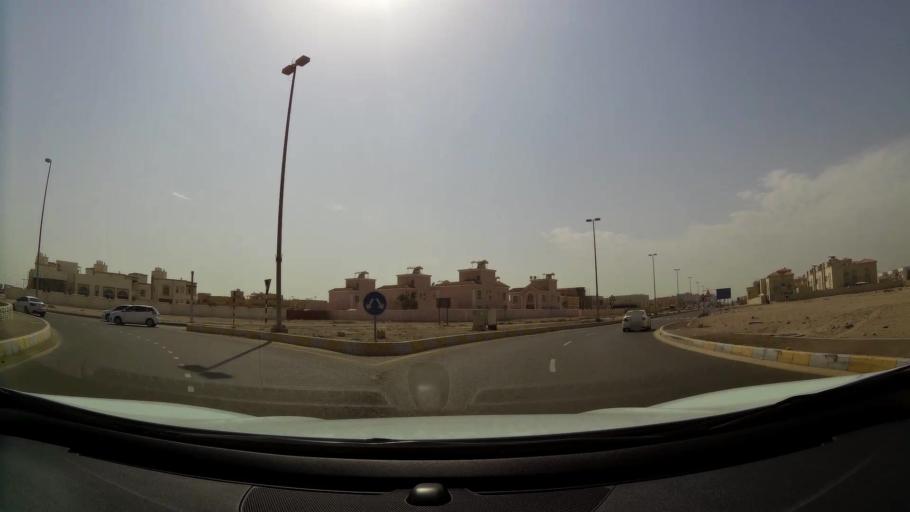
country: AE
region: Abu Dhabi
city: Abu Dhabi
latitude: 24.3388
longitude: 54.5481
